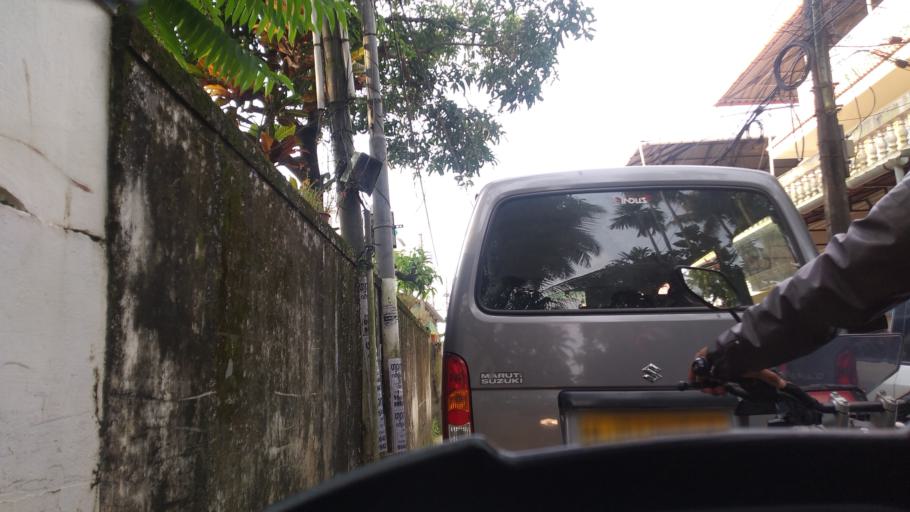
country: IN
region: Kerala
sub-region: Ernakulam
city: Cochin
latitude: 9.9834
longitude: 76.3096
